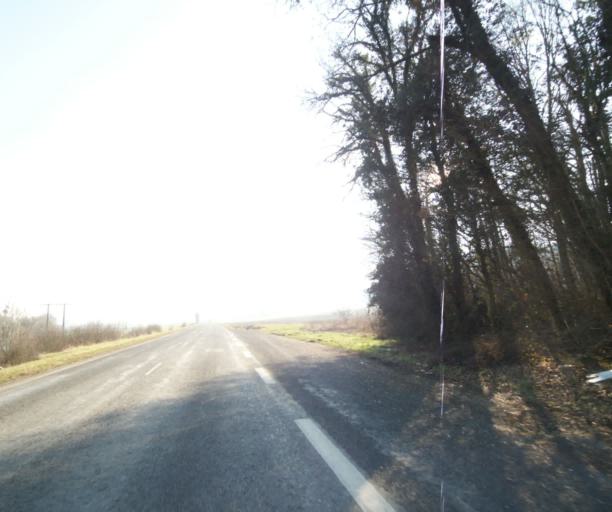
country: FR
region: Champagne-Ardenne
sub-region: Departement de la Haute-Marne
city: Chevillon
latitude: 48.5151
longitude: 5.1102
